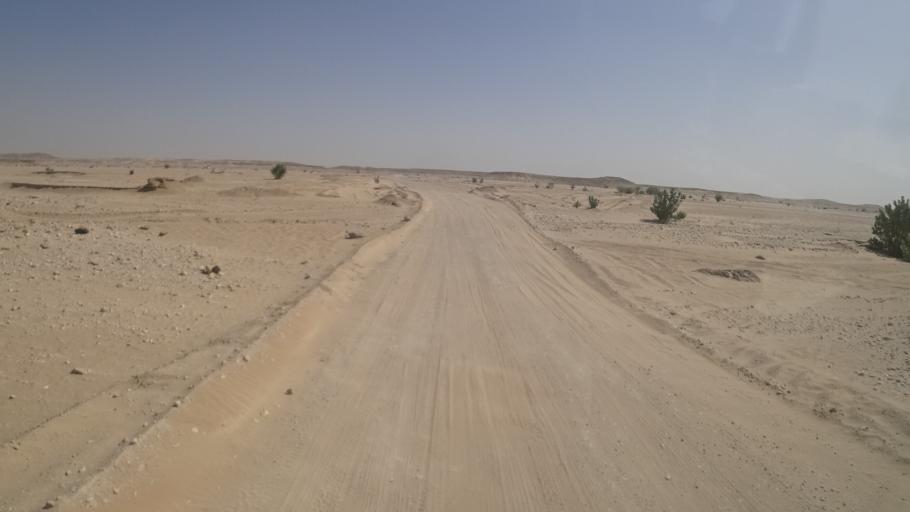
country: YE
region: Al Mahrah
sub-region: Shahan
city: Shihan as Sufla
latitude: 17.8766
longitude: 52.6054
